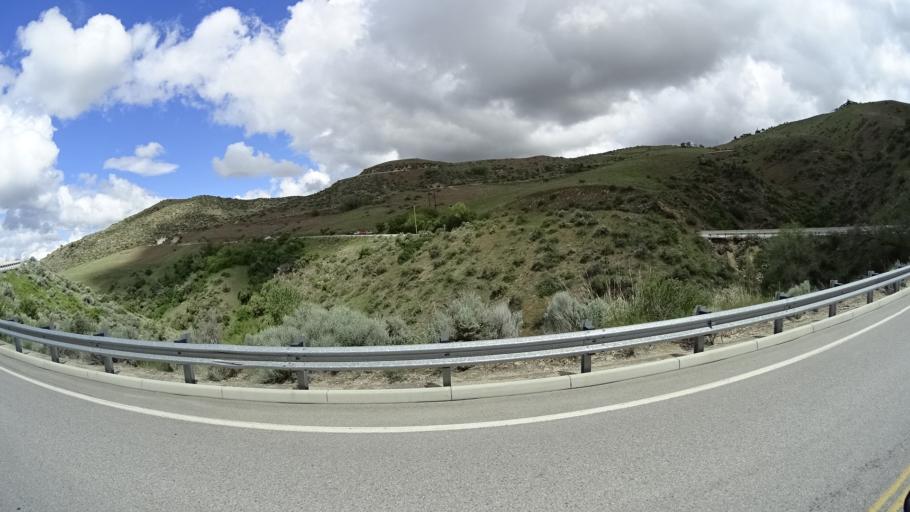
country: US
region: Idaho
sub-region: Ada County
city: Boise
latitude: 43.6867
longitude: -116.1806
